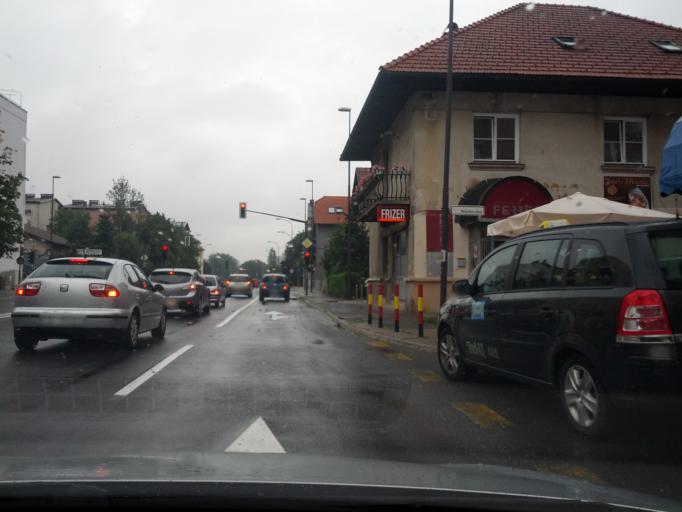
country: SI
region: Ljubljana
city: Ljubljana
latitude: 46.0669
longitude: 14.4957
